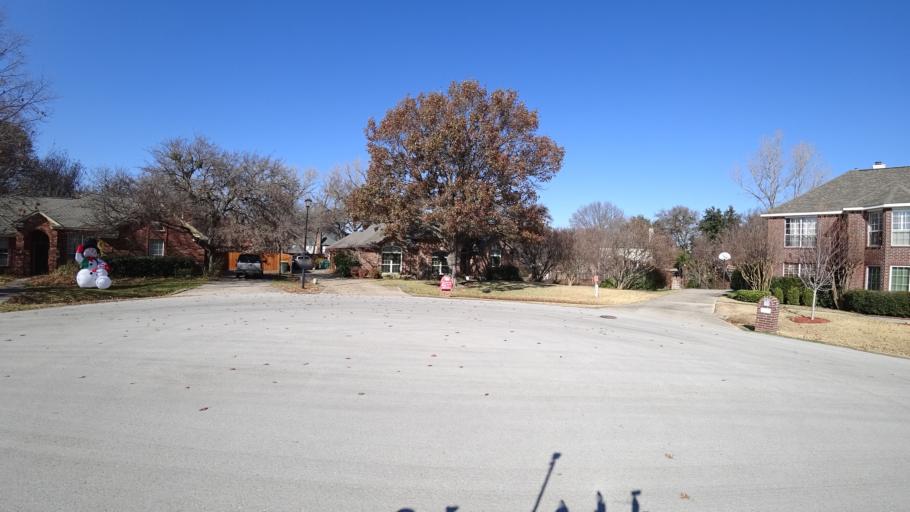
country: US
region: Texas
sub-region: Denton County
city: Lewisville
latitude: 33.0157
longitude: -97.0209
